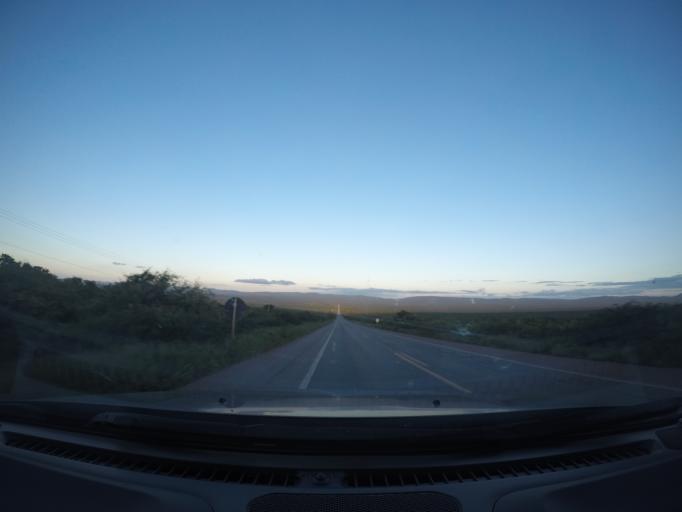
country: BR
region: Bahia
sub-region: Seabra
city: Seabra
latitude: -12.4125
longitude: -41.9753
